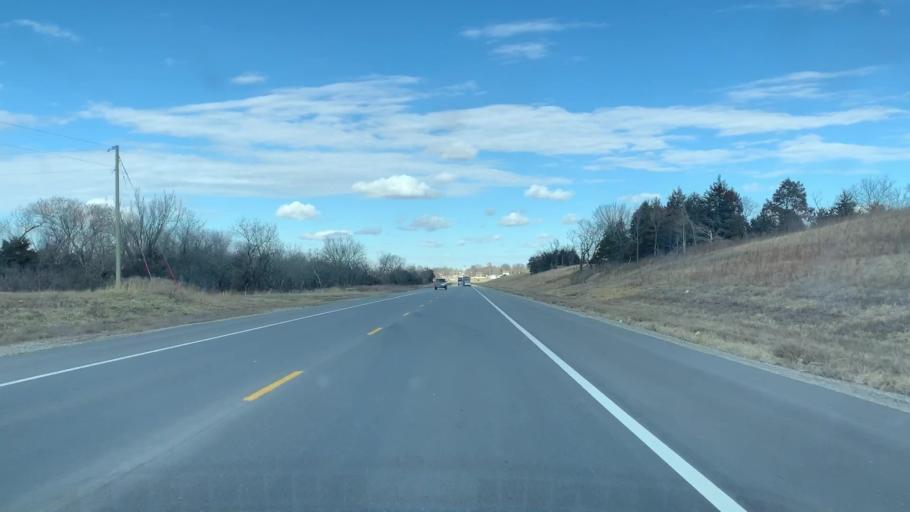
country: US
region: Kansas
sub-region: Crawford County
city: Pittsburg
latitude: 37.3306
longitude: -94.8321
